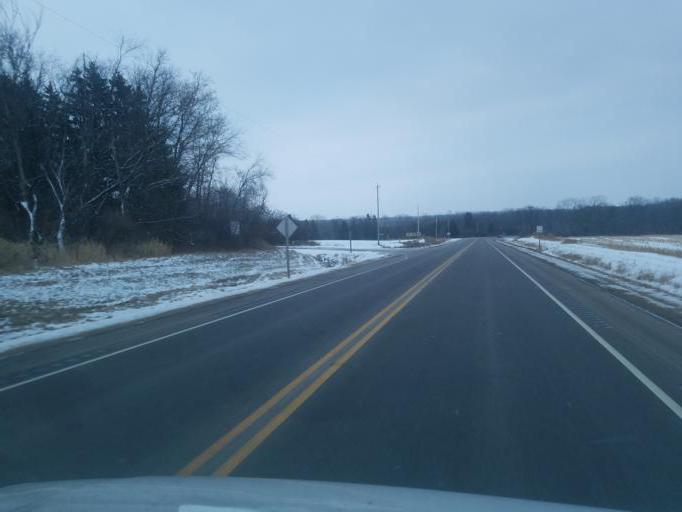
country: US
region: Wisconsin
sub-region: Waupaca County
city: New London
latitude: 44.4098
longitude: -88.7915
